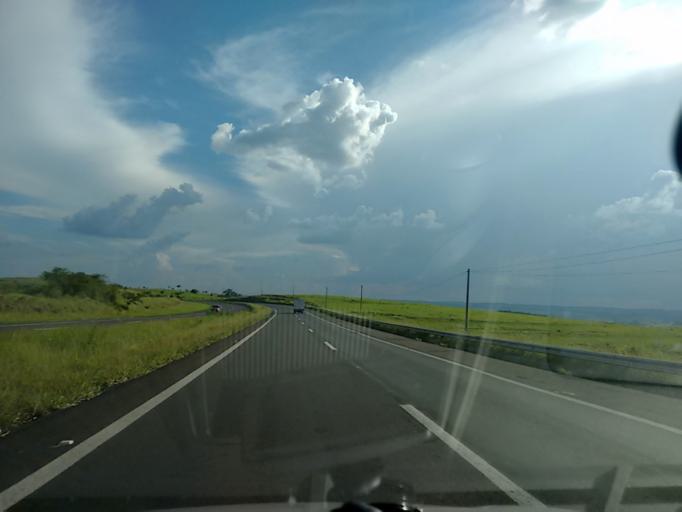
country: BR
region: Sao Paulo
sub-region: Duartina
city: Duartina
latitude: -22.2927
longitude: -49.4956
